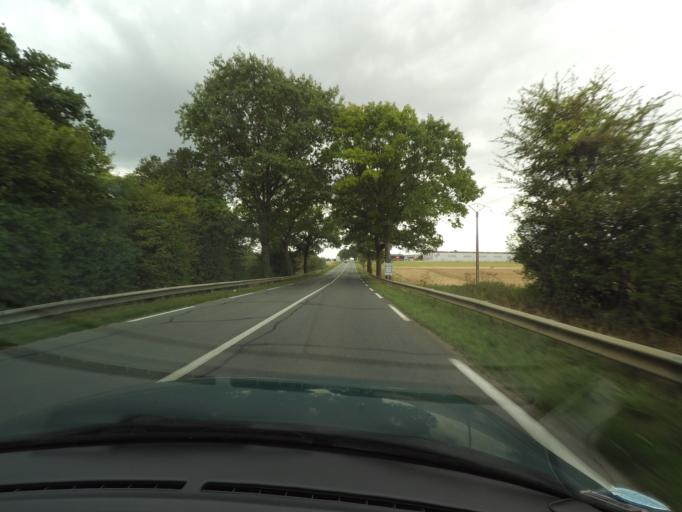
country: FR
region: Poitou-Charentes
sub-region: Departement de la Vienne
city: Ayron
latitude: 46.6587
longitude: 0.0867
